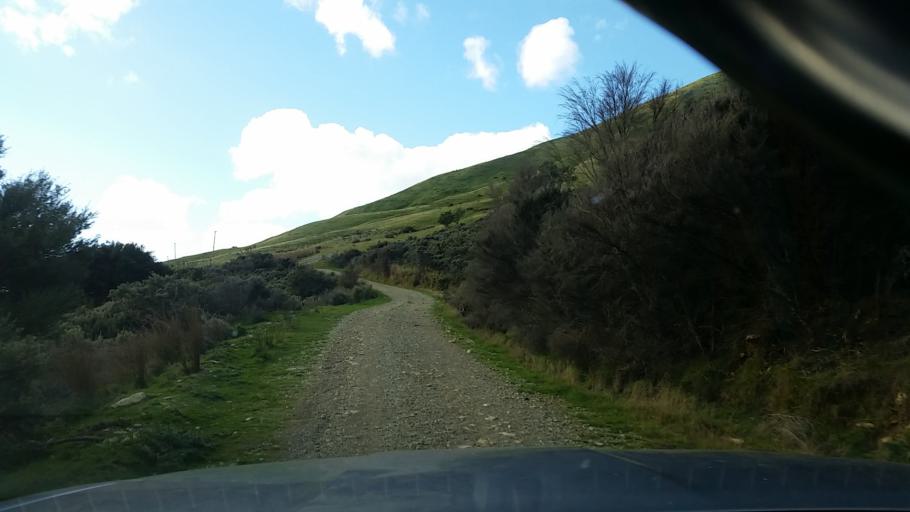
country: NZ
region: Marlborough
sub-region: Marlborough District
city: Picton
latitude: -41.0533
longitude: 174.1097
